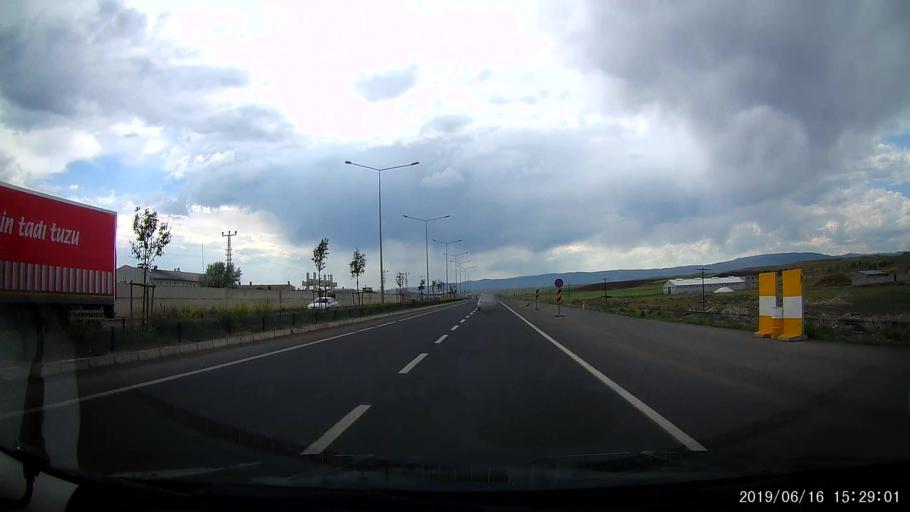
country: TR
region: Erzurum
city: Horasan
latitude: 40.0311
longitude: 42.1414
